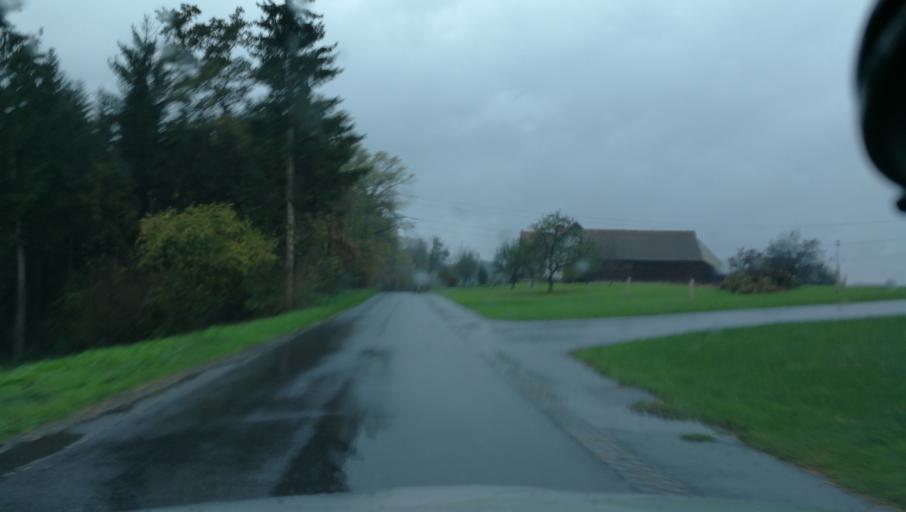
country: AT
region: Styria
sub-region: Politischer Bezirk Leibnitz
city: Strass in Steiermark
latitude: 46.7357
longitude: 15.6532
